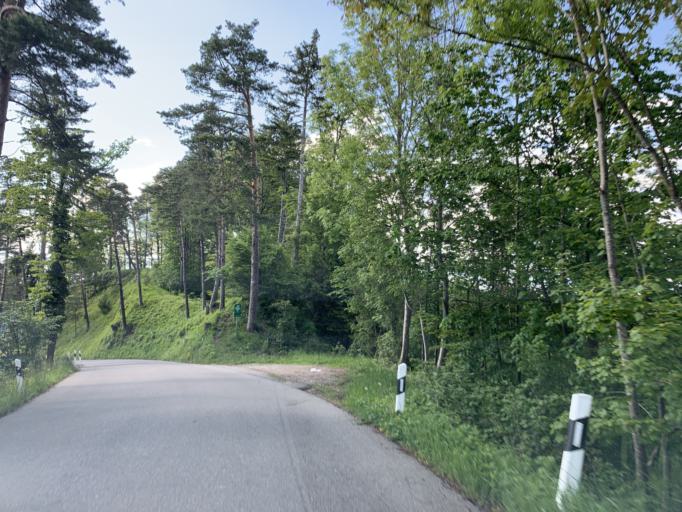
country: CH
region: Zurich
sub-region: Bezirk Winterthur
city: Mattenbach (Kreis 7)
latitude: 47.4591
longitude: 8.7420
